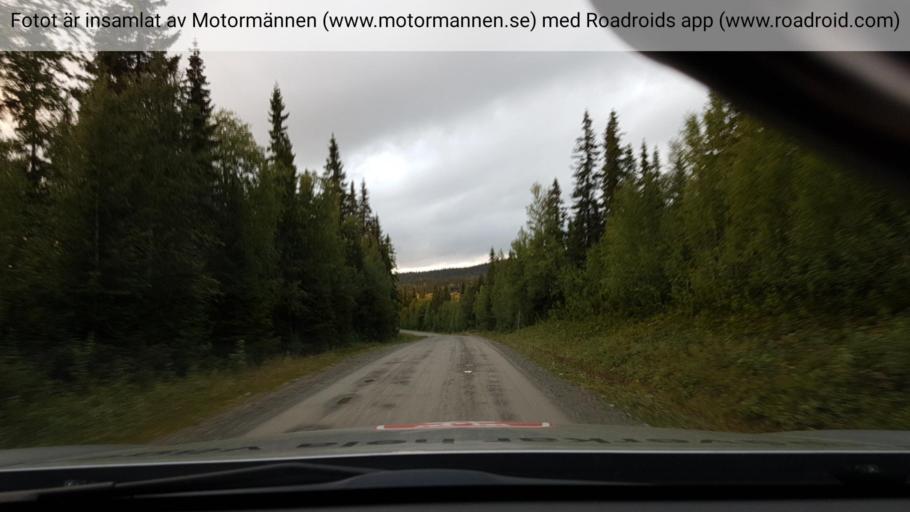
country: SE
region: Vaesterbotten
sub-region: Vilhelmina Kommun
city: Sjoberg
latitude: 65.5506
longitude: 15.4139
